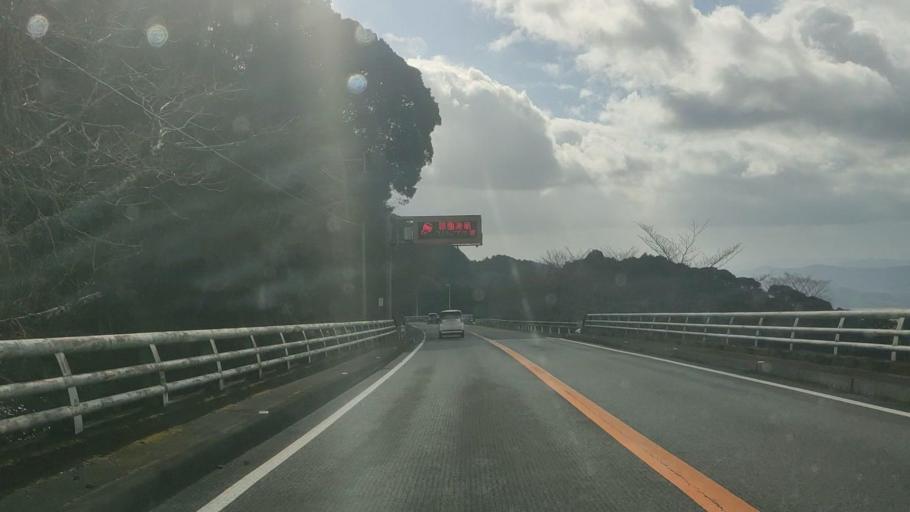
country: JP
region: Kumamoto
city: Hitoyoshi
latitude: 32.0864
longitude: 130.8011
